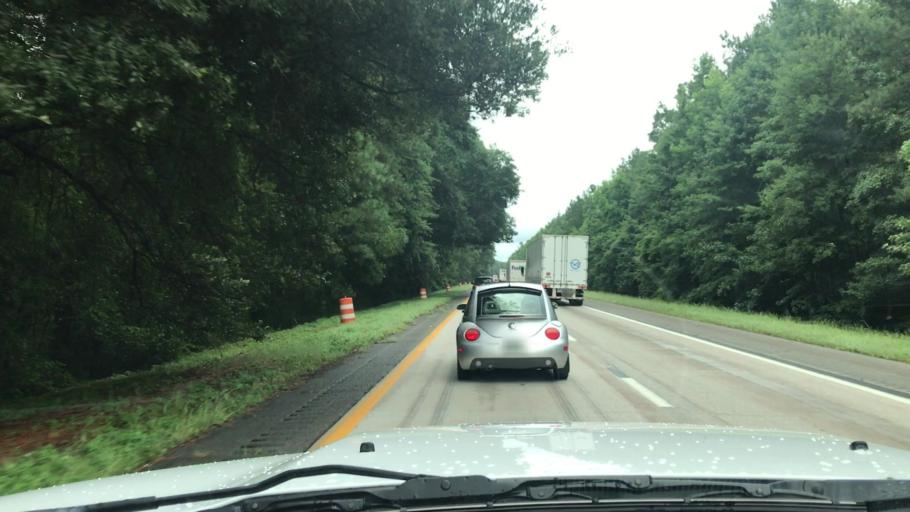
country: US
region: South Carolina
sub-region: Jasper County
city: Ridgeland
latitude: 32.4090
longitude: -81.0147
